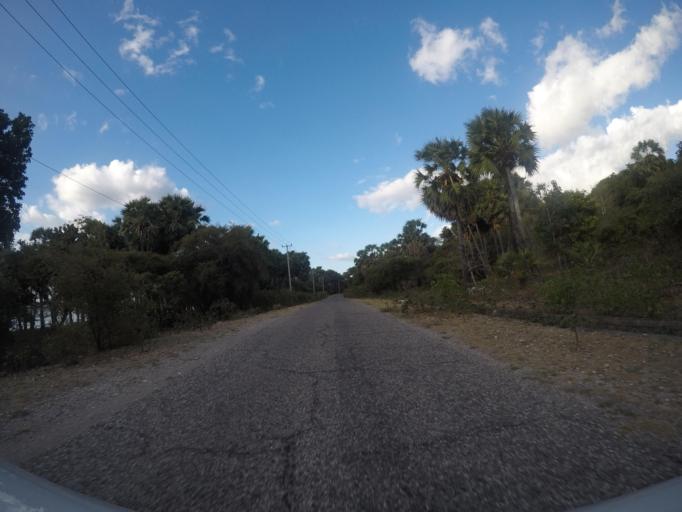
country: TL
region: Lautem
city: Lospalos
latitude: -8.3435
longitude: 126.9283
